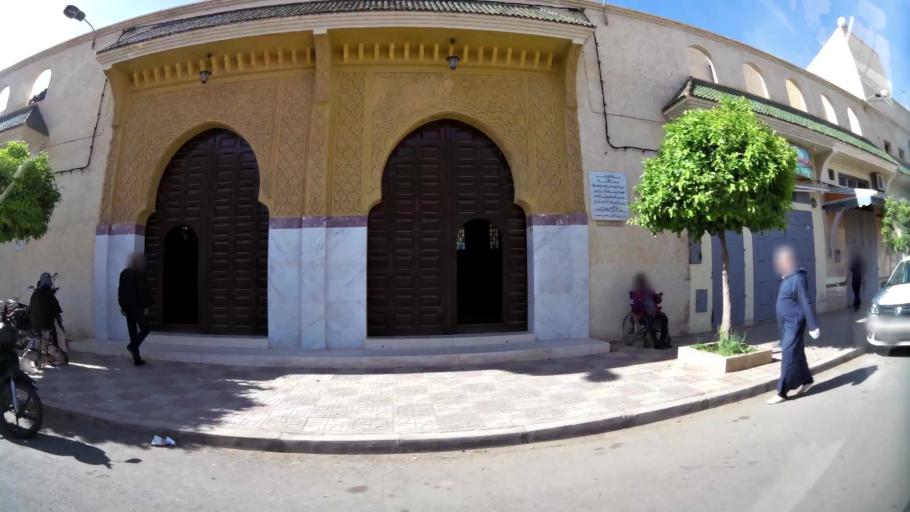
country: MA
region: Oriental
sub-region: Oujda-Angad
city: Oujda
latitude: 34.6707
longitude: -1.9083
